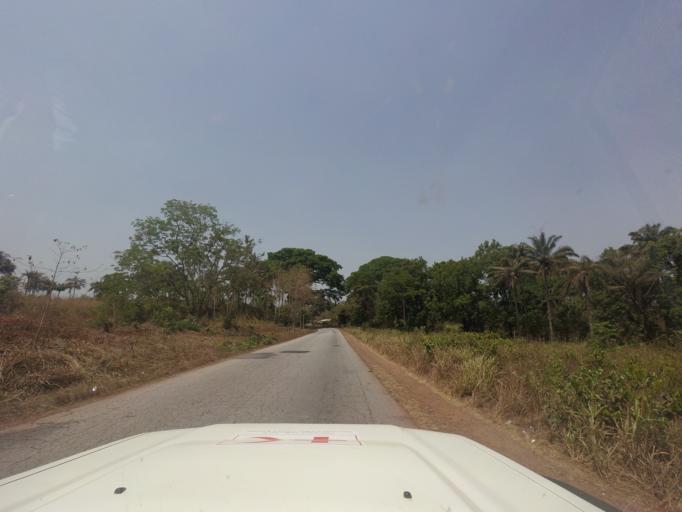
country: GN
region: Kindia
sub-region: Kindia
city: Kindia
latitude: 9.9015
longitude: -13.0446
